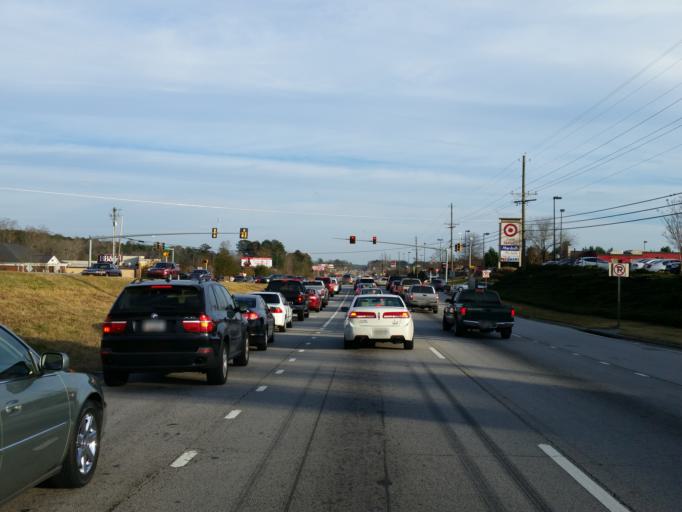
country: US
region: Georgia
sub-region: Paulding County
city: Hiram
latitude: 33.8887
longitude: -84.7463
